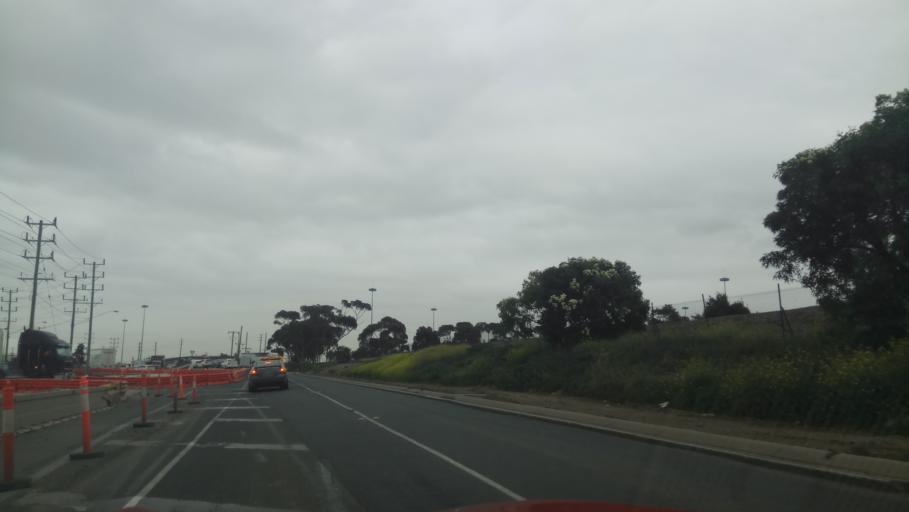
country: AU
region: Victoria
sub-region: Brimbank
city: Brooklyn
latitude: -37.8309
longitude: 144.8194
